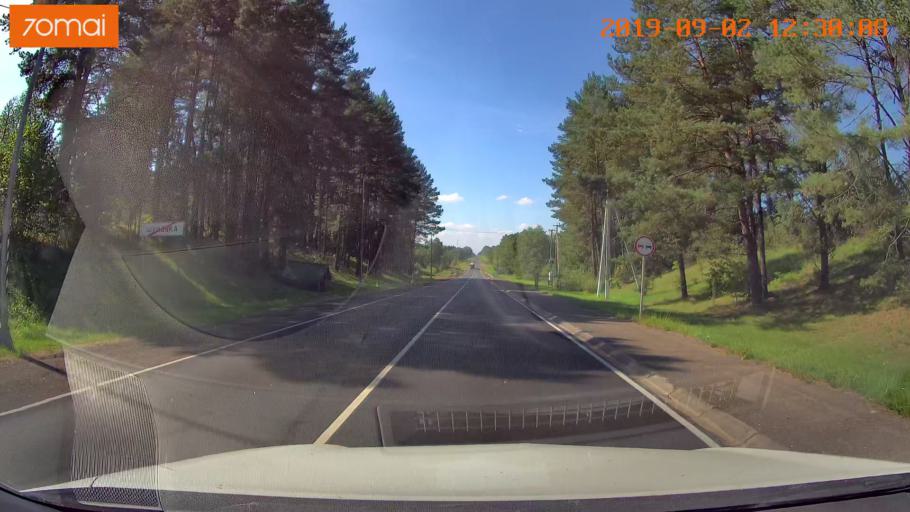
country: RU
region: Smolensk
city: Shumyachi
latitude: 53.8340
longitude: 32.4808
